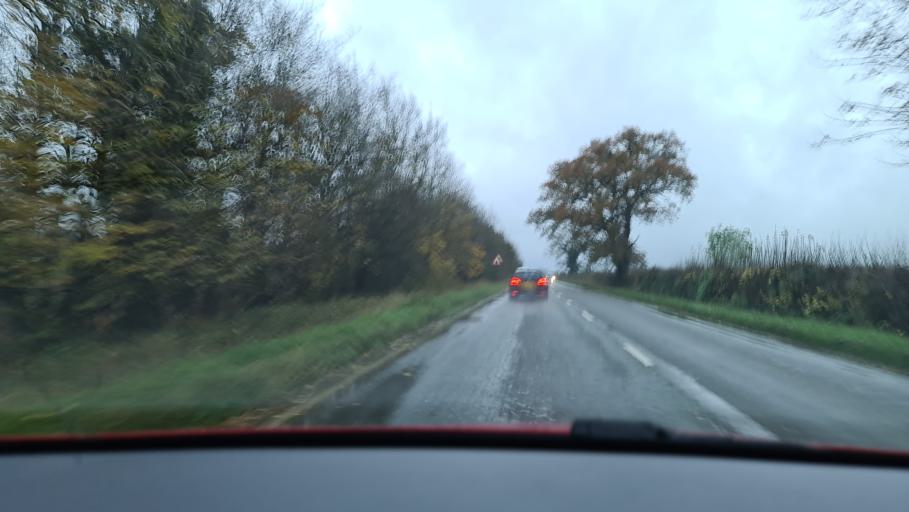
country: GB
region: England
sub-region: Oxfordshire
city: Somerton
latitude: 51.9301
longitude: -1.2176
